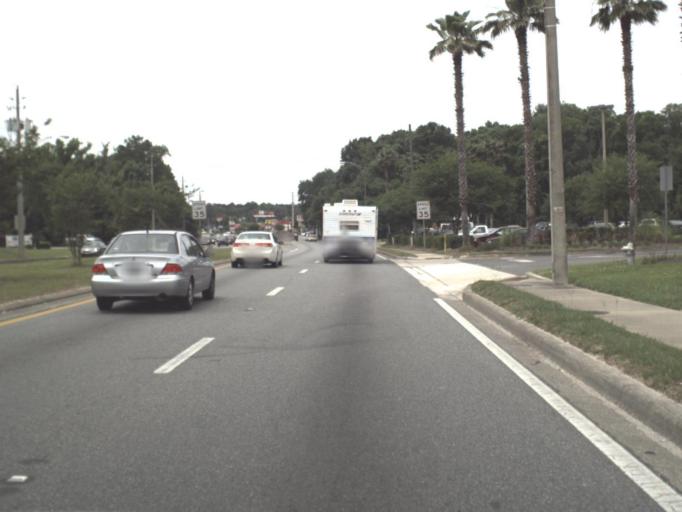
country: US
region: Florida
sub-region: Clay County
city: Middleburg
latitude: 30.0644
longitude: -81.8711
